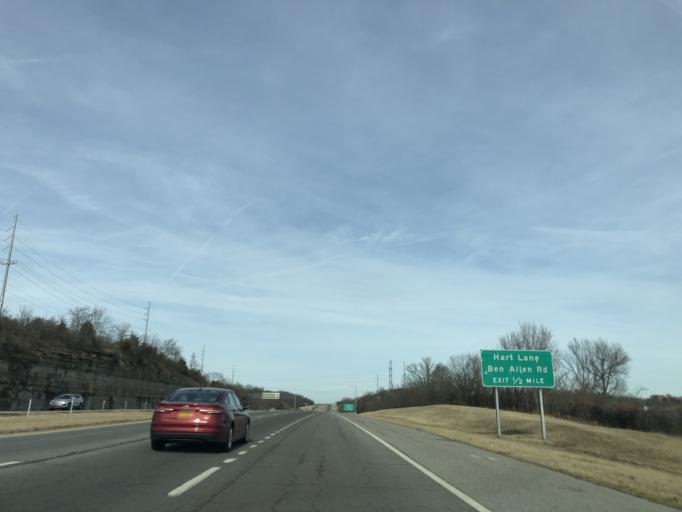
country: US
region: Tennessee
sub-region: Davidson County
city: Nashville
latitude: 36.2076
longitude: -86.7494
